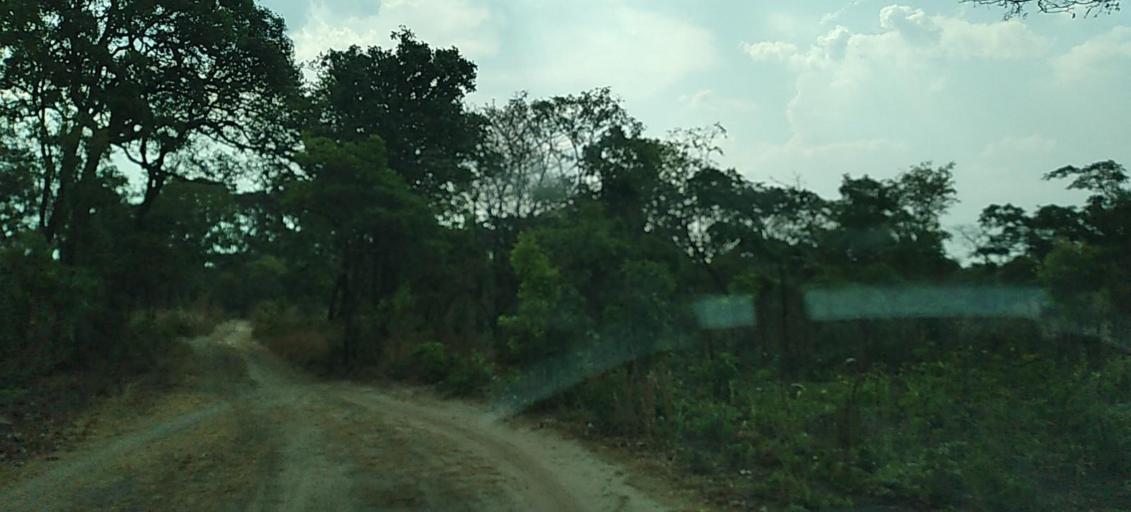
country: ZM
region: North-Western
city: Solwezi
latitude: -12.0972
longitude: 26.2809
